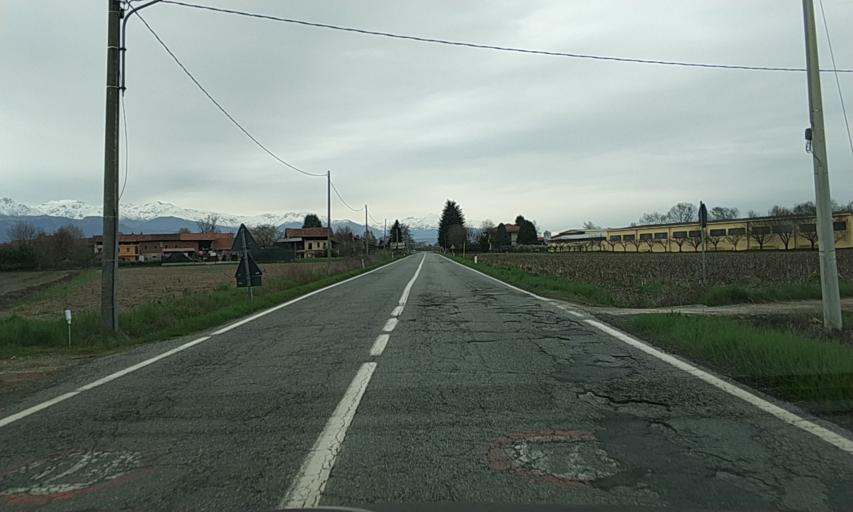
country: IT
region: Piedmont
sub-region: Provincia di Torino
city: Favria
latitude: 45.3146
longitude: 7.6791
